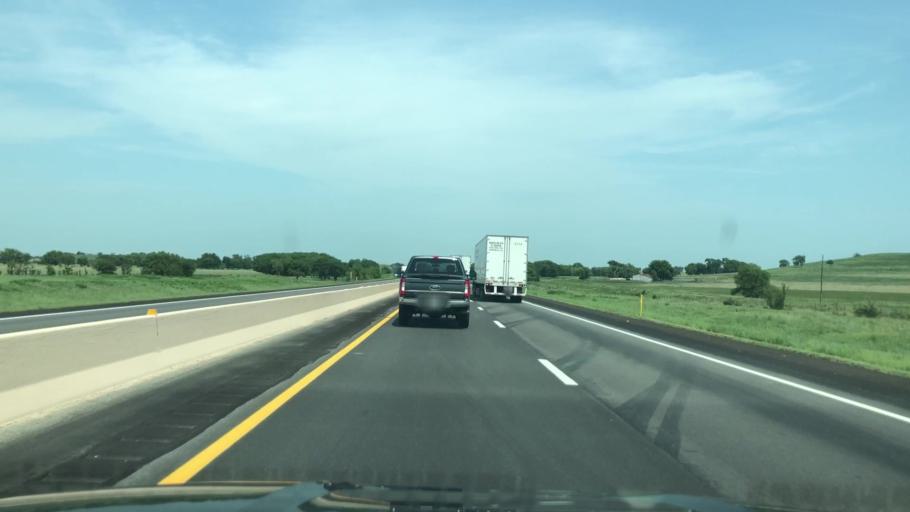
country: US
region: Oklahoma
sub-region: Ottawa County
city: Afton
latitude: 36.6837
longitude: -95.0353
